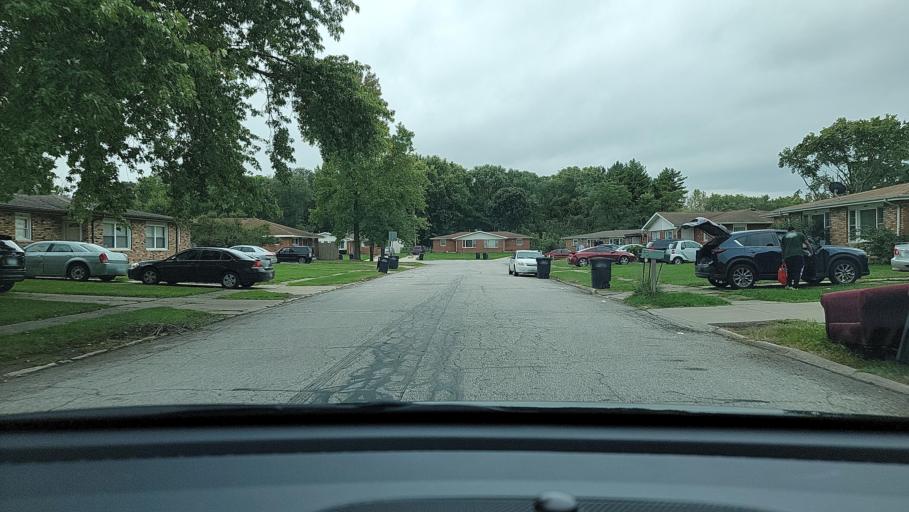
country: US
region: Indiana
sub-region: Porter County
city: Portage
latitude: 41.5555
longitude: -87.2064
